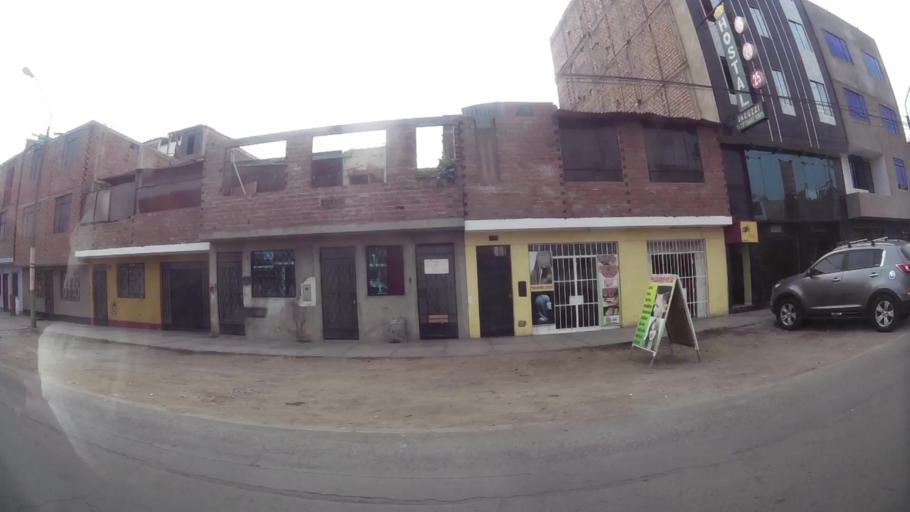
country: PE
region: Callao
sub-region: Callao
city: Callao
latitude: -12.0264
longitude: -77.1000
